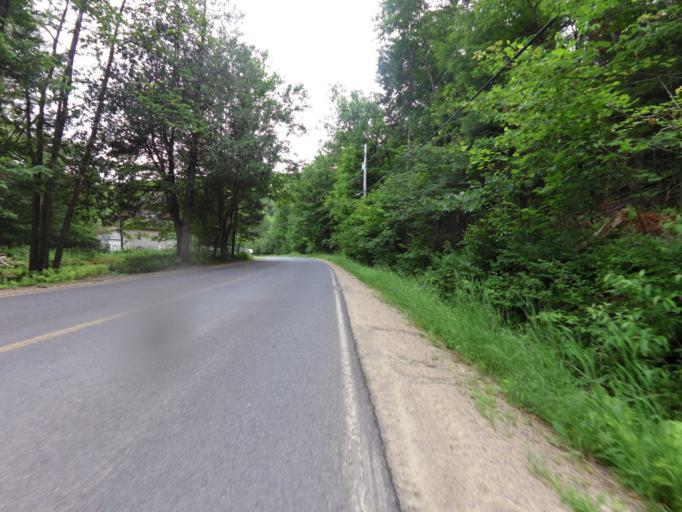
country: CA
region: Quebec
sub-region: Laurentides
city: Brownsburg-Chatham
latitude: 45.8959
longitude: -74.6022
